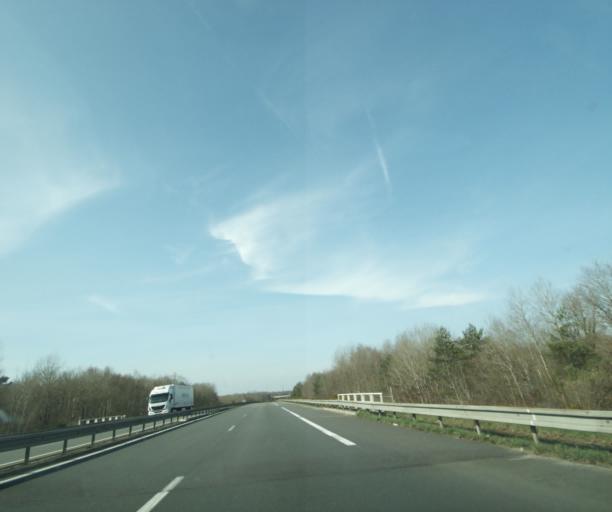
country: FR
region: Centre
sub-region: Departement du Loir-et-Cher
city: Salbris
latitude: 47.4356
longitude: 2.0117
